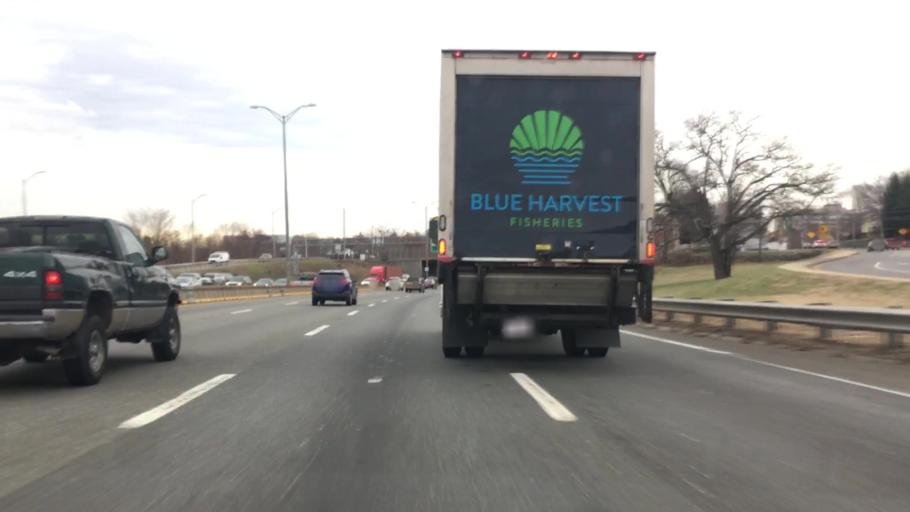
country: US
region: Massachusetts
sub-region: Norfolk County
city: Quincy
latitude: 42.2442
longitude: -71.0303
